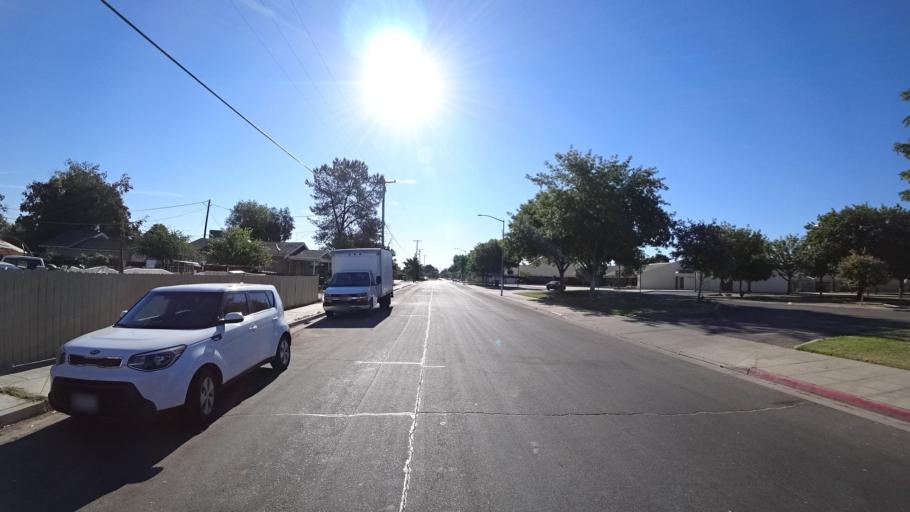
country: US
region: California
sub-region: Fresno County
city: Fresno
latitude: 36.7533
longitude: -119.7656
